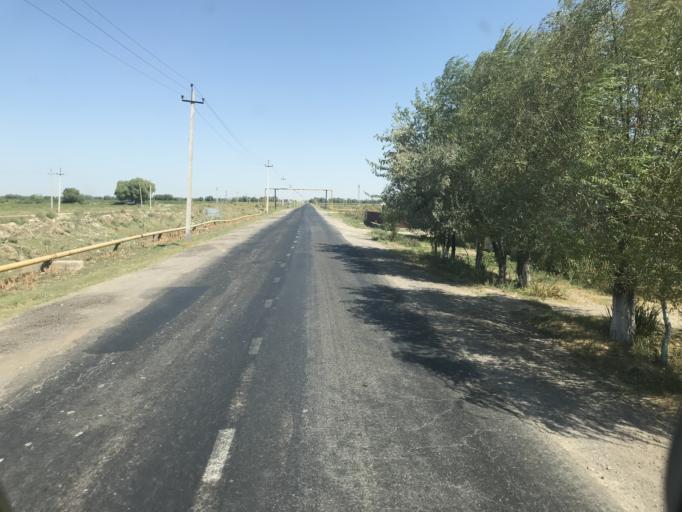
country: KZ
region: Ongtustik Qazaqstan
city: Ilyich
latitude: 40.9009
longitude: 68.4882
